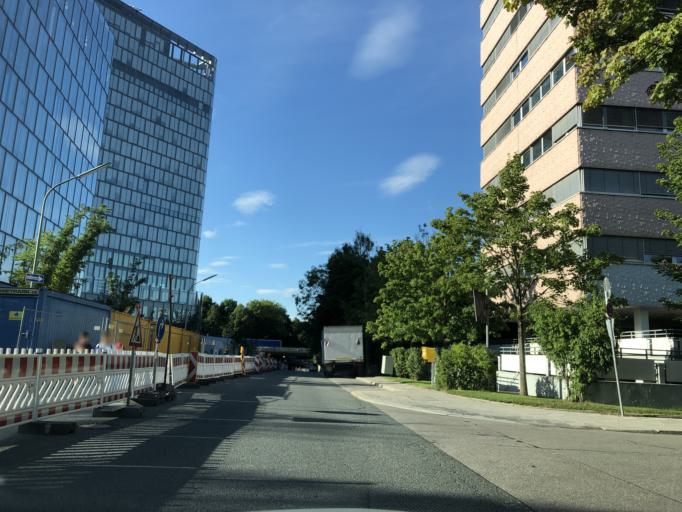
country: DE
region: Bavaria
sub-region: Upper Bavaria
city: Bogenhausen
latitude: 48.1366
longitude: 11.6244
